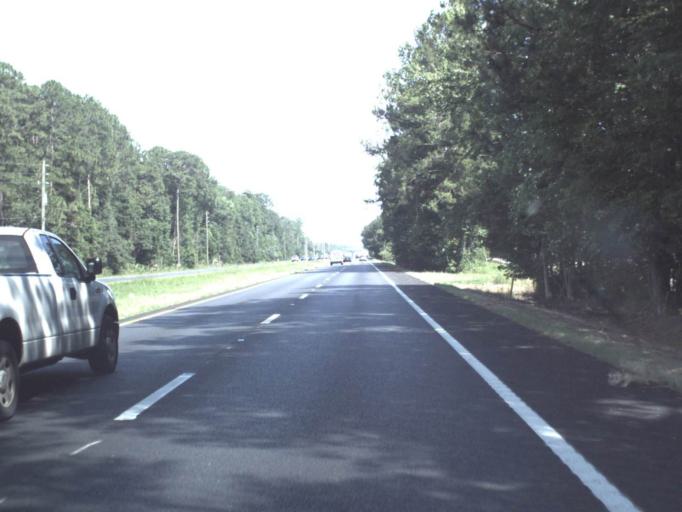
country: US
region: Florida
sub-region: Saint Johns County
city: Palm Valley
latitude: 30.1112
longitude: -81.4858
